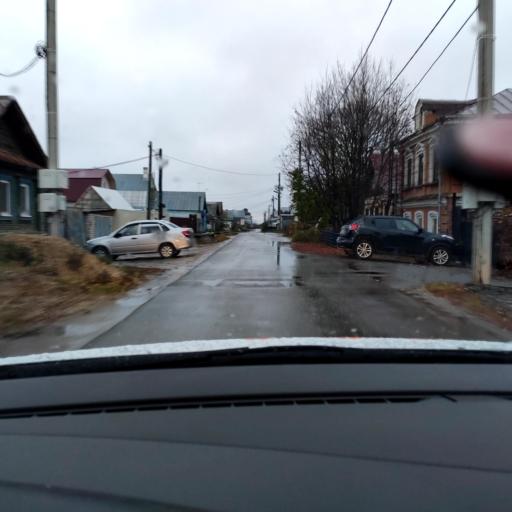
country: RU
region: Tatarstan
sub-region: Gorod Kazan'
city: Kazan
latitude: 55.7955
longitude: 49.0573
